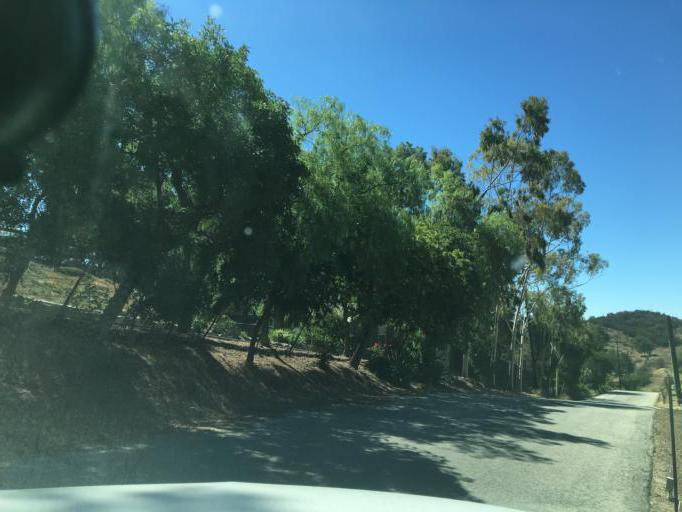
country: US
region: California
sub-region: Los Angeles County
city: Malibu
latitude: 34.0740
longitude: -118.8984
